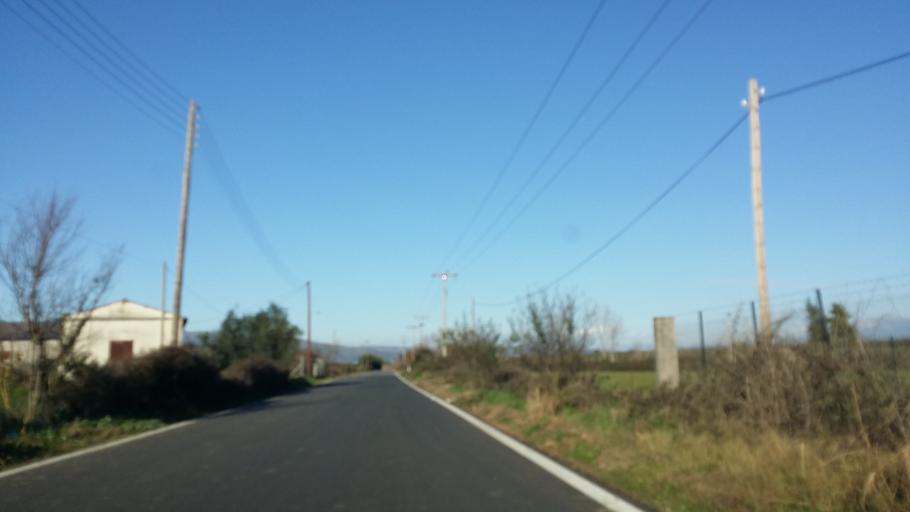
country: GR
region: West Greece
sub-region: Nomos Aitolias kai Akarnanias
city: Angelokastro
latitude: 38.6190
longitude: 21.2279
